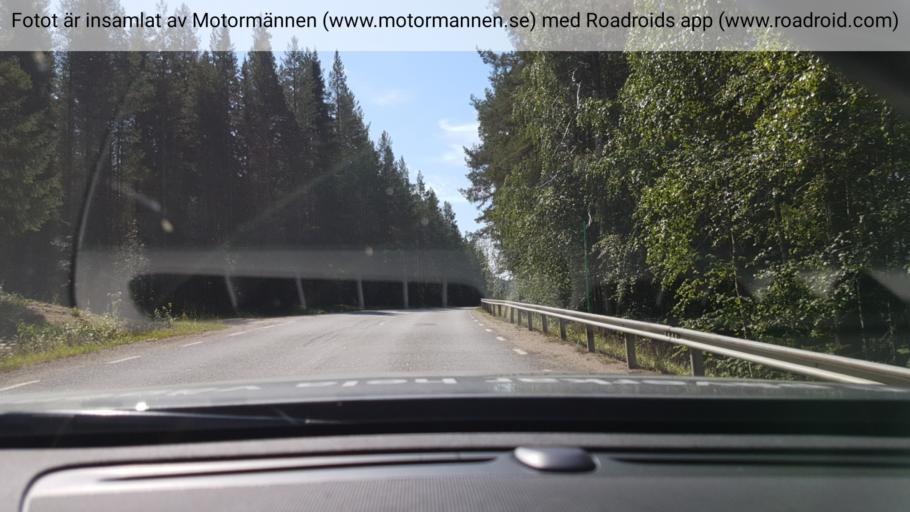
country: SE
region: Vaesterbotten
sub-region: Vindelns Kommun
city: Vindeln
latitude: 64.2633
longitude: 19.6321
